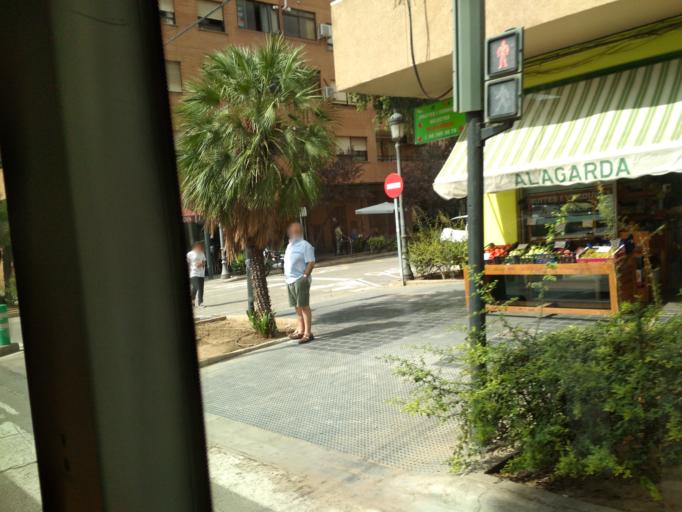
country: ES
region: Valencia
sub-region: Provincia de Valencia
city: Valencia
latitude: 39.4548
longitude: -0.3758
